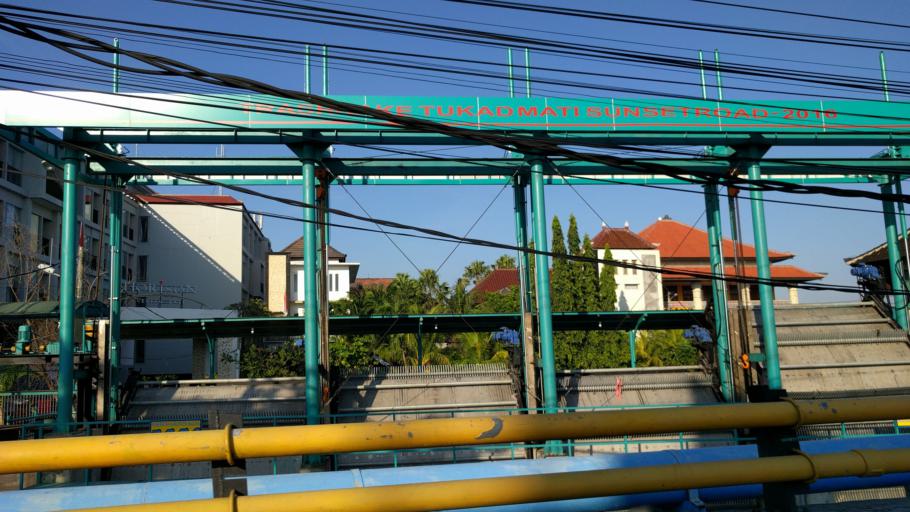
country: ID
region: Bali
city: Kuta
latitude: -8.6965
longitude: 115.1762
